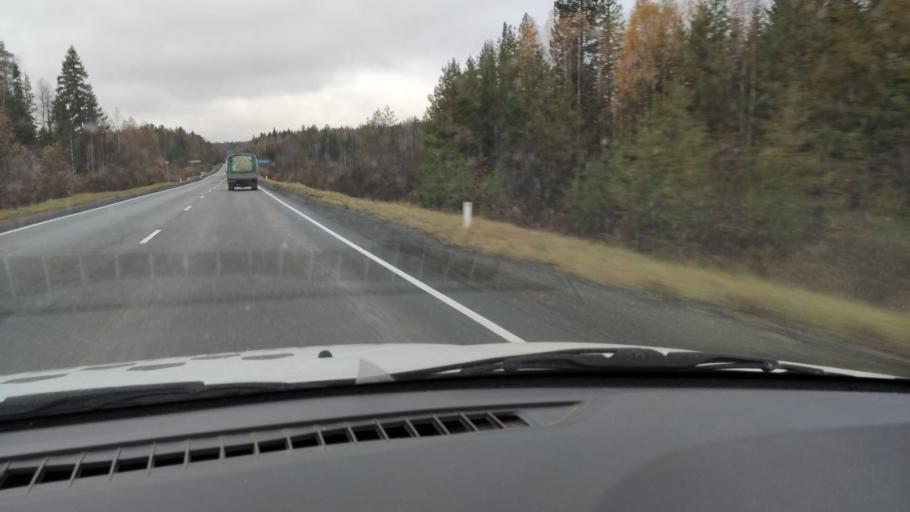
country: RU
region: Kirov
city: Dubrovka
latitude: 58.9053
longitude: 51.2681
